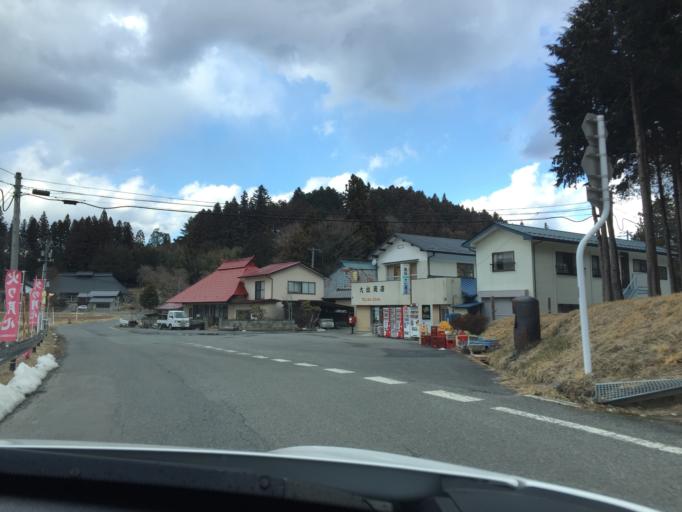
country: JP
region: Fukushima
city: Iwaki
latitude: 37.2436
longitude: 140.7277
